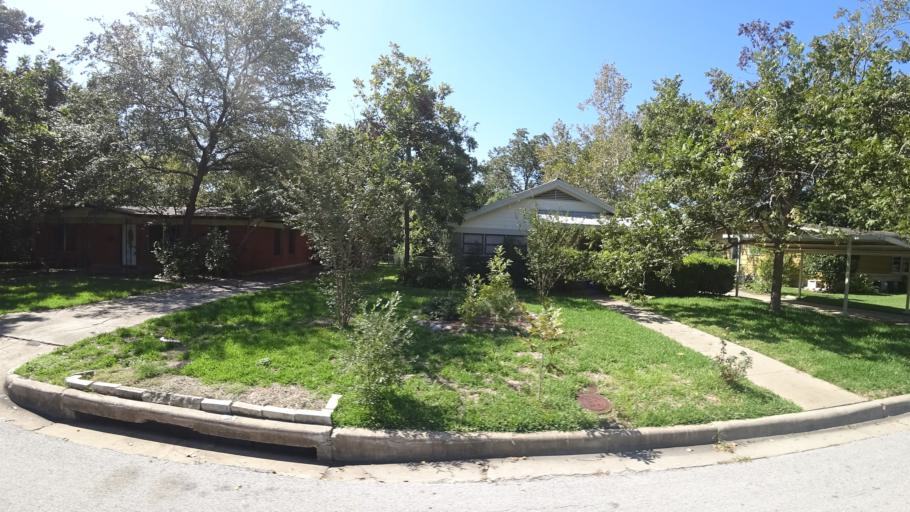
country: US
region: Texas
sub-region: Travis County
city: Austin
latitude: 30.3142
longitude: -97.7021
